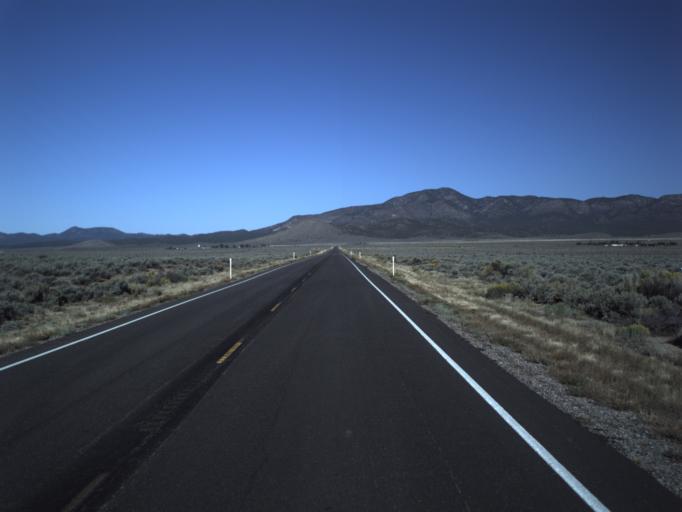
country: US
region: Utah
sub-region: Washington County
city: Enterprise
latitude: 37.7894
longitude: -113.8844
